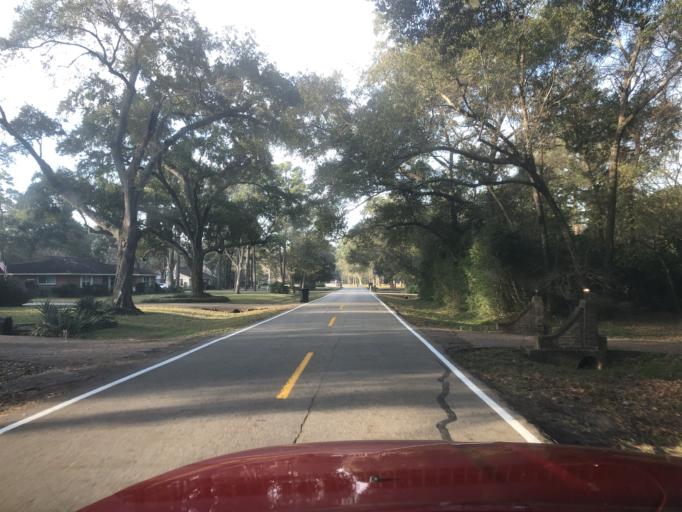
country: US
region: Texas
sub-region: Harris County
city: Spring
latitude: 30.0181
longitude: -95.4743
